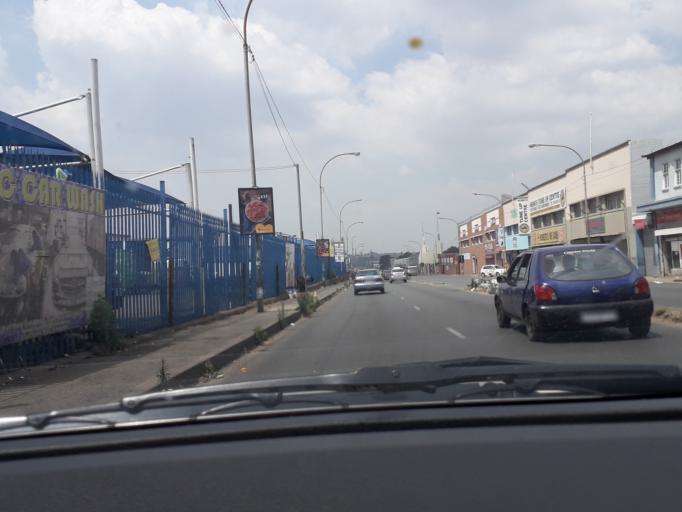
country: ZA
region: Gauteng
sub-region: City of Johannesburg Metropolitan Municipality
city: Johannesburg
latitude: -26.2162
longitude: 28.0437
